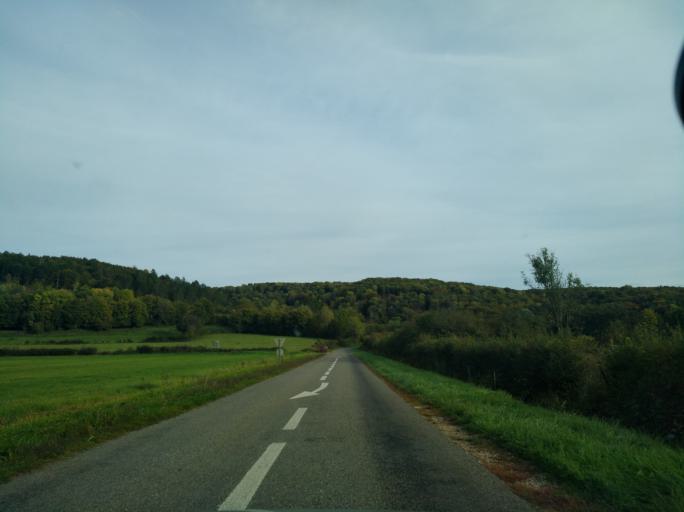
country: FR
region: Bourgogne
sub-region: Departement de Saone-et-Loire
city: Cuiseaux
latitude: 46.4830
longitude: 5.4672
